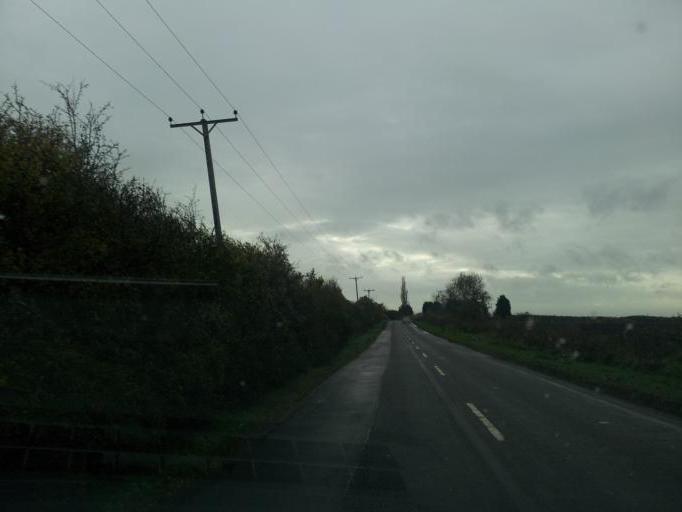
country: GB
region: England
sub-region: Nottinghamshire
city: Newark on Trent
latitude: 53.0363
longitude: -0.7981
